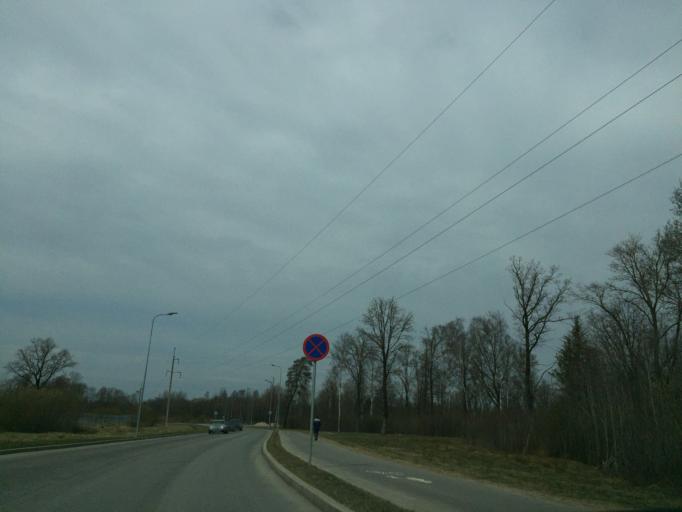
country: EE
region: Ida-Virumaa
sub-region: Narva linn
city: Narva
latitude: 59.3965
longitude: 28.1784
